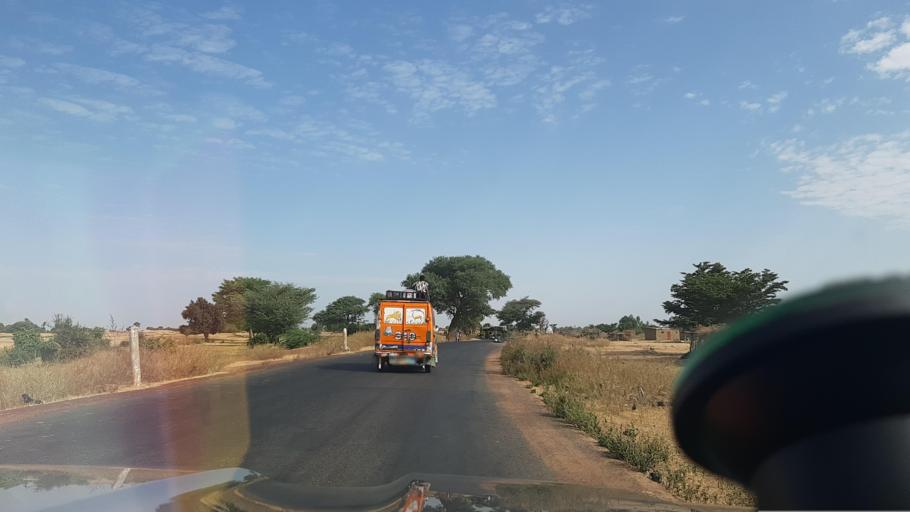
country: ML
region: Segou
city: Markala
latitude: 13.6911
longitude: -6.1004
